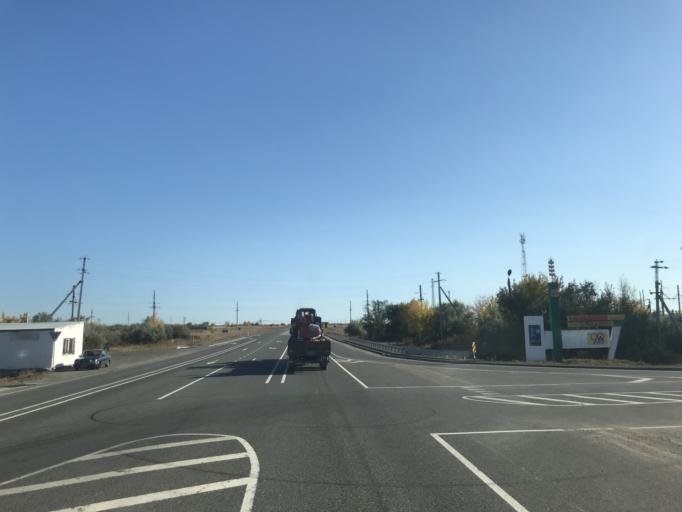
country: KZ
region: Pavlodar
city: Koktobe
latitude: 51.9262
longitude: 77.3342
